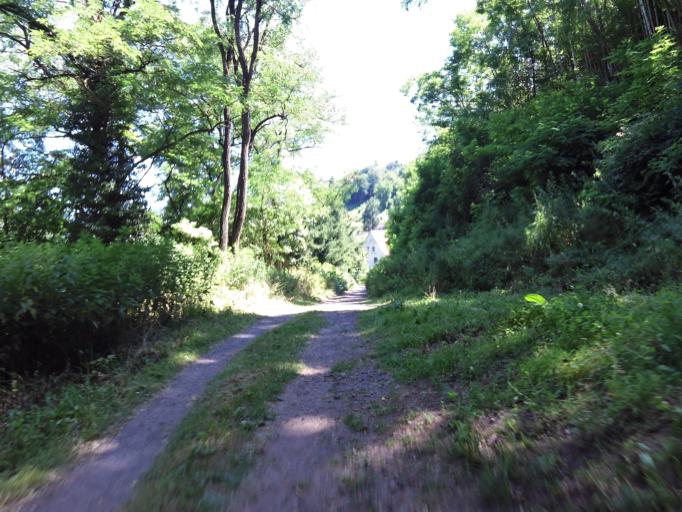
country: DE
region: Rheinland-Pfalz
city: Frankeneck
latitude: 49.3735
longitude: 8.0587
